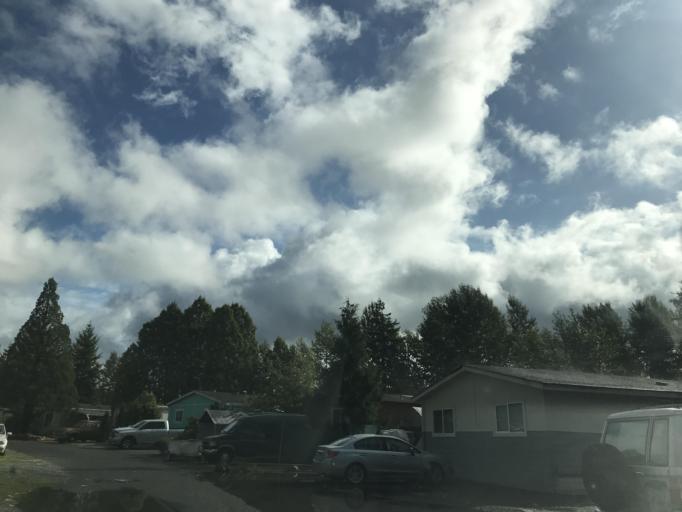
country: US
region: Washington
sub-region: Whatcom County
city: Bellingham
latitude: 48.7865
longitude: -122.4981
